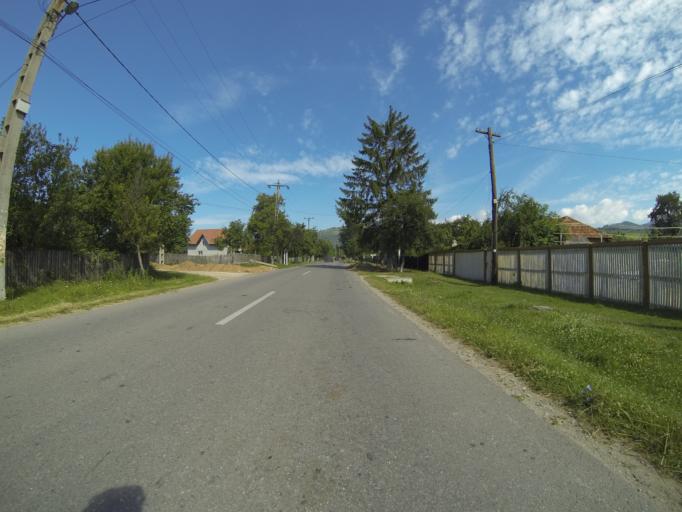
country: RO
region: Gorj
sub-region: Comuna Polovragi
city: Polovragi
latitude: 45.1743
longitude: 23.8008
